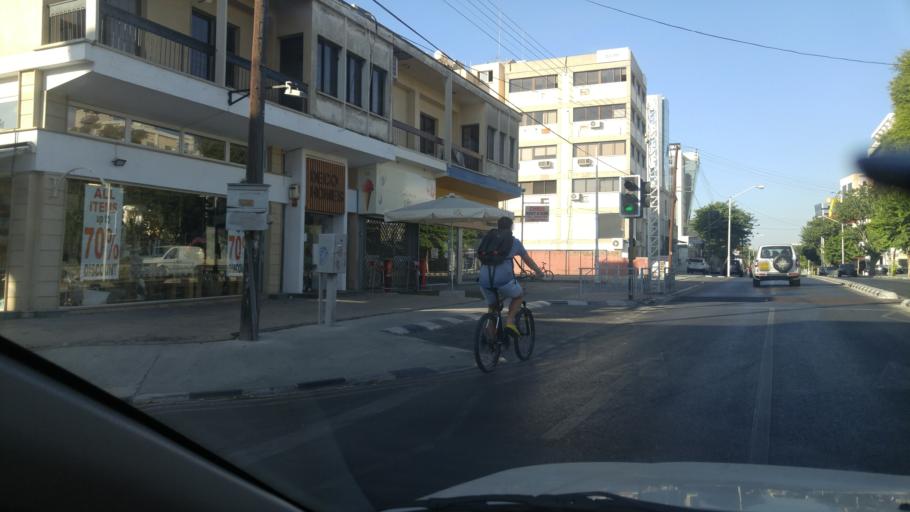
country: CY
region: Limassol
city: Limassol
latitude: 34.6875
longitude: 33.0423
